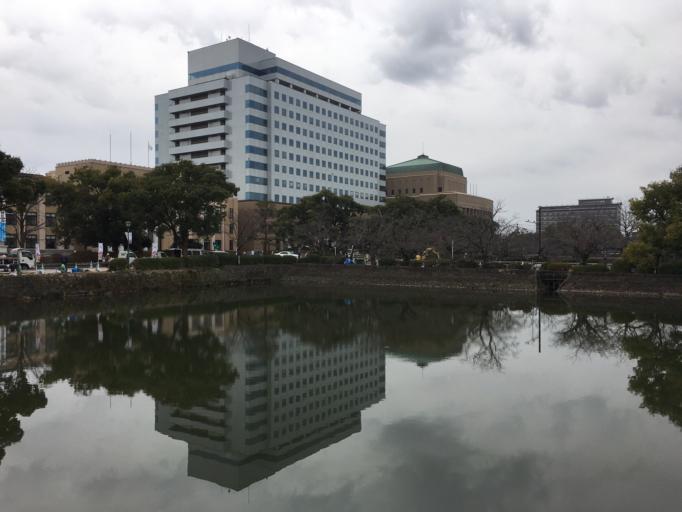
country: JP
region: Saga Prefecture
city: Saga-shi
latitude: 33.2507
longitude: 130.3001
